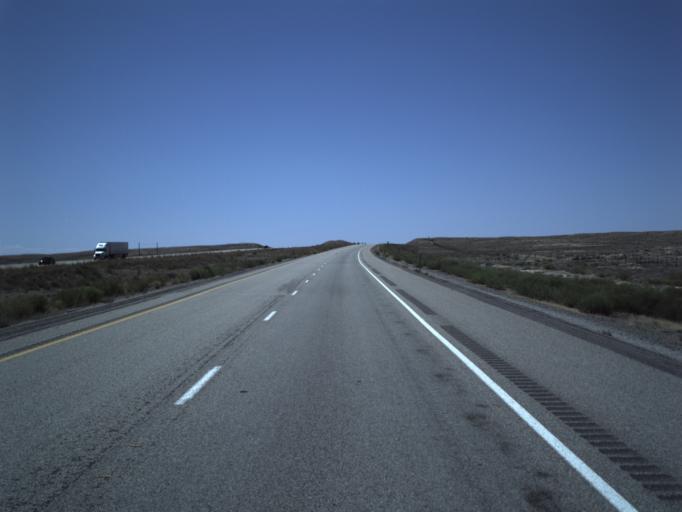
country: US
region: Utah
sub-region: Grand County
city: Moab
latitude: 39.0114
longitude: -109.3075
